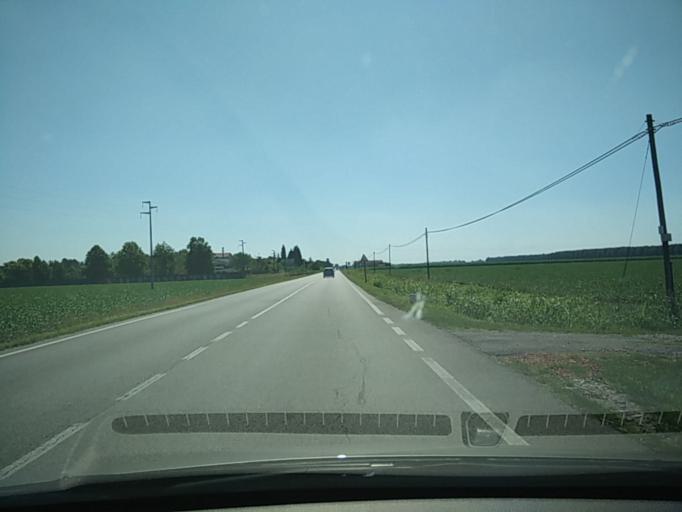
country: IT
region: Veneto
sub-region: Provincia di Venezia
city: San Dona di Piave
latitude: 45.6400
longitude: 12.6168
